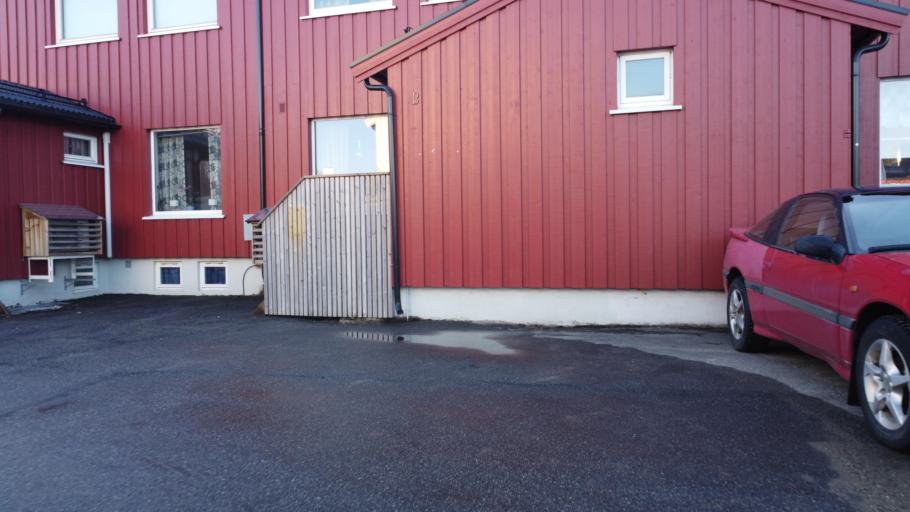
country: NO
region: Nordland
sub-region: Rana
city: Mo i Rana
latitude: 66.3162
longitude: 14.1583
